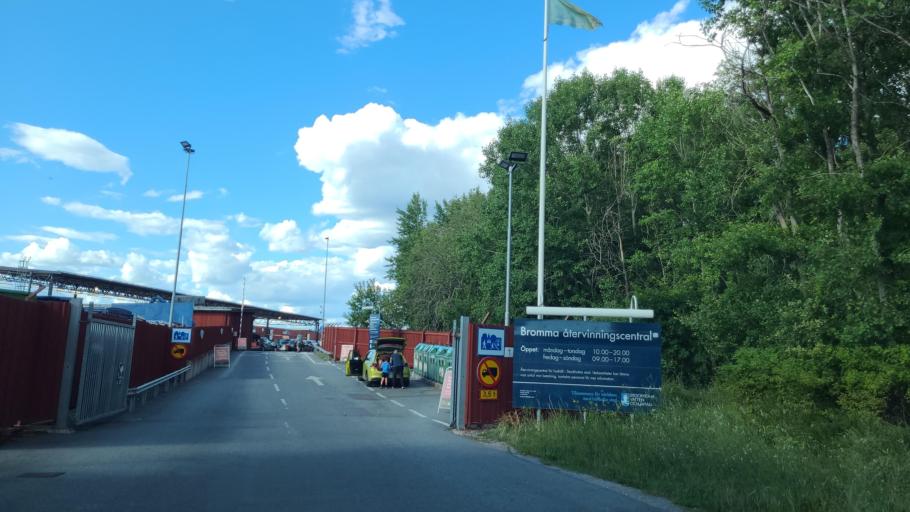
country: SE
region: Stockholm
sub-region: Stockholms Kommun
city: Bromma
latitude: 59.3479
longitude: 17.9499
